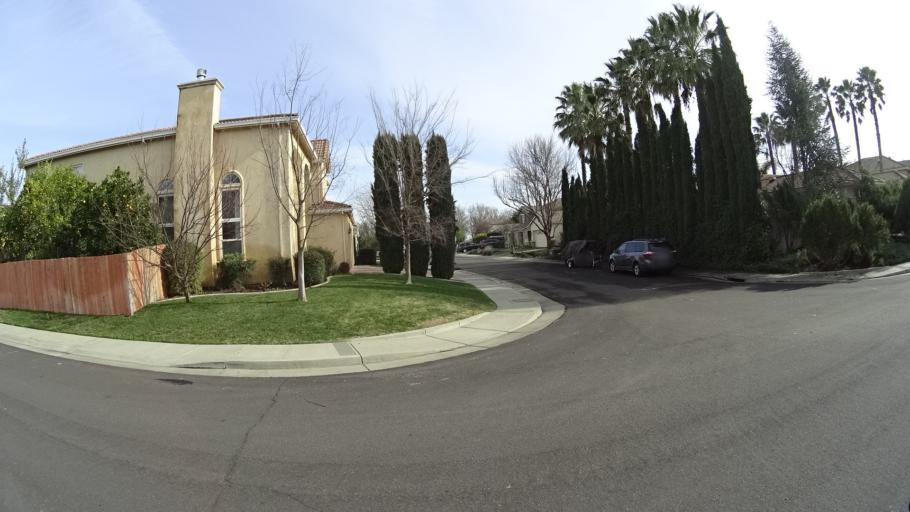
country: US
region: California
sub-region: Yolo County
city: Davis
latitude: 38.5514
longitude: -121.6773
